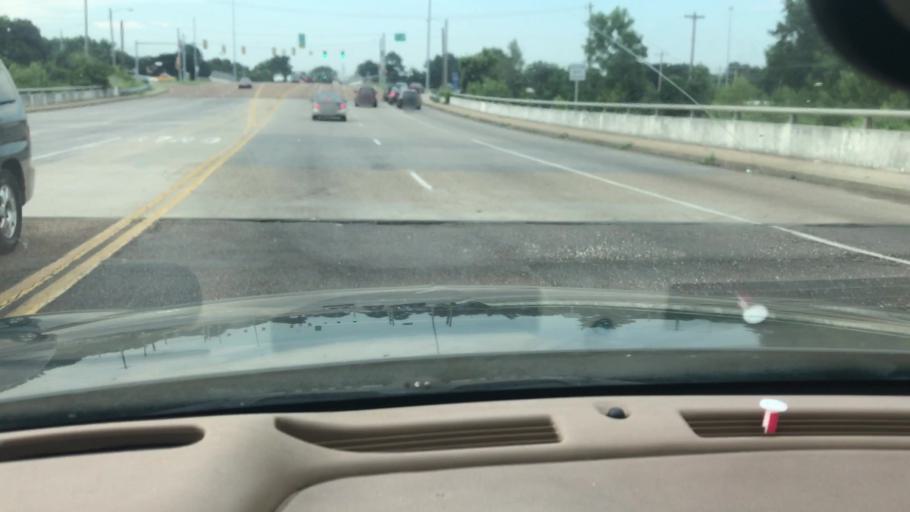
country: US
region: Tennessee
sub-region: Shelby County
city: Germantown
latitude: 35.0762
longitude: -89.9064
